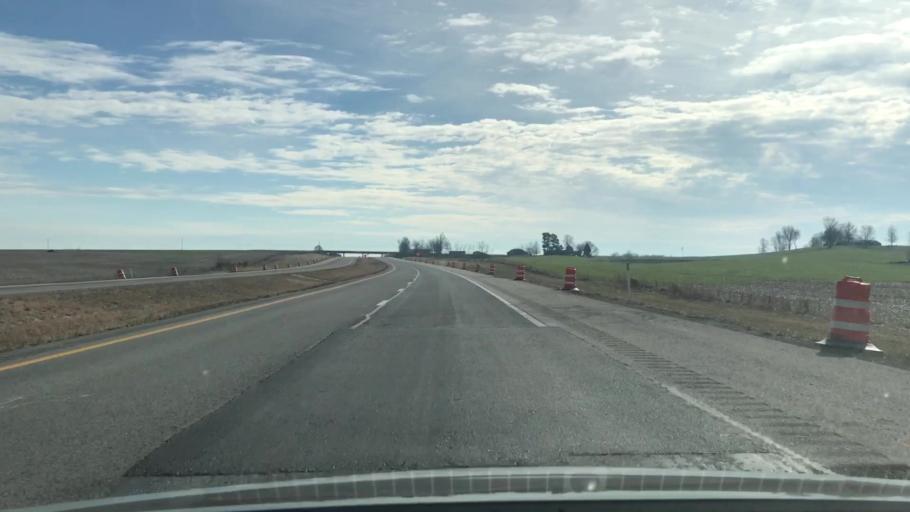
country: US
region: Kentucky
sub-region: Daviess County
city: Masonville
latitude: 37.6668
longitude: -87.0213
